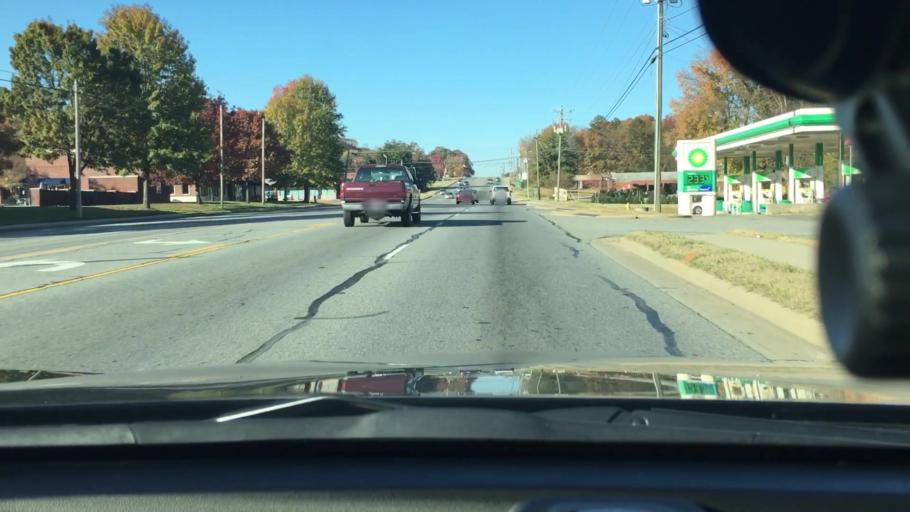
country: US
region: North Carolina
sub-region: Cabarrus County
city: Harrisburg
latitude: 35.3222
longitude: -80.6504
